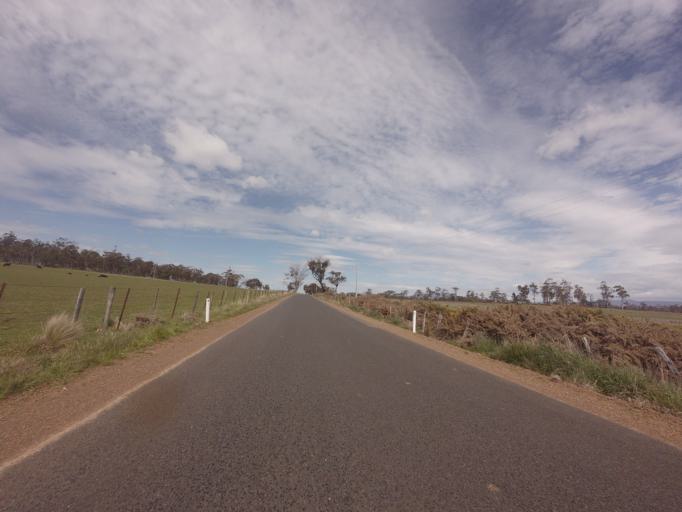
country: AU
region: Tasmania
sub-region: Northern Midlands
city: Longford
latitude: -41.7251
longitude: 147.1915
